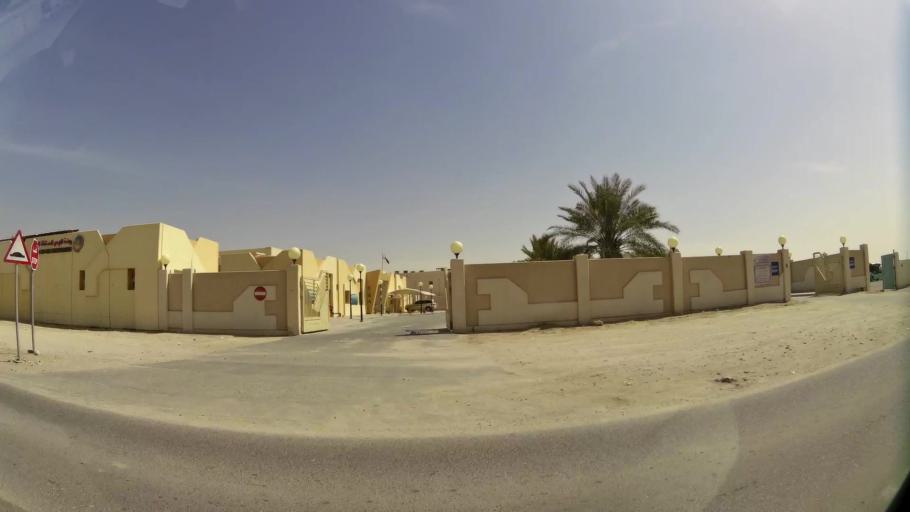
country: QA
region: Baladiyat ar Rayyan
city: Ar Rayyan
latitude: 25.2642
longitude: 51.4069
